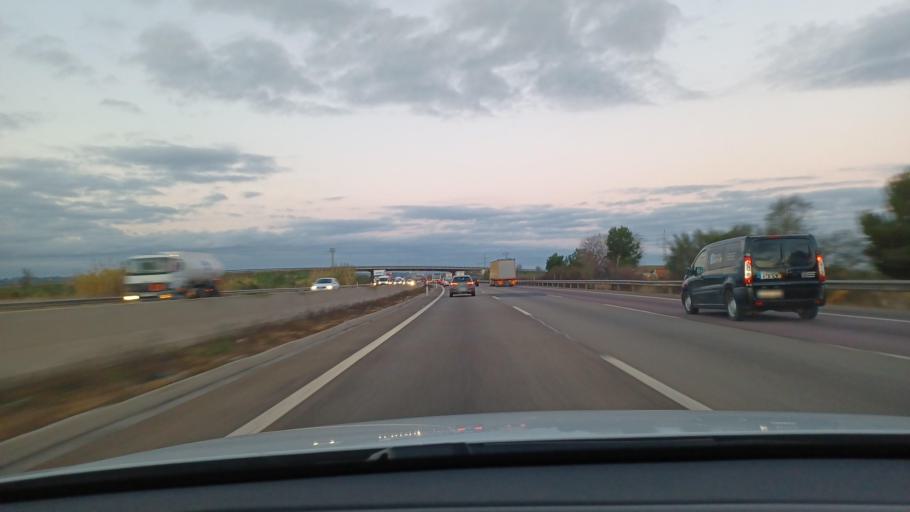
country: ES
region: Valencia
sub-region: Provincia de Valencia
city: Moncada
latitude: 39.5857
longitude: -0.4047
